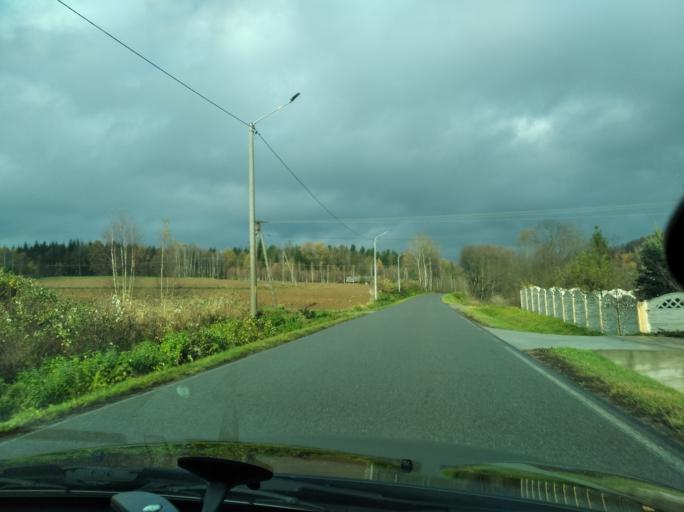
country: PL
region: Subcarpathian Voivodeship
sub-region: Powiat strzyzowski
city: Wisniowa
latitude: 49.9248
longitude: 21.7161
